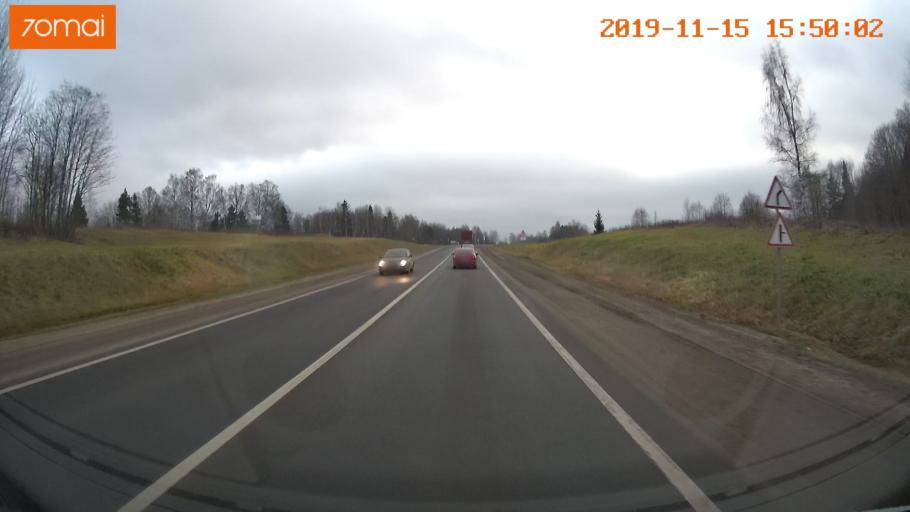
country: RU
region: Jaroslavl
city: Yaroslavl
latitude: 57.9095
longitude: 40.0120
